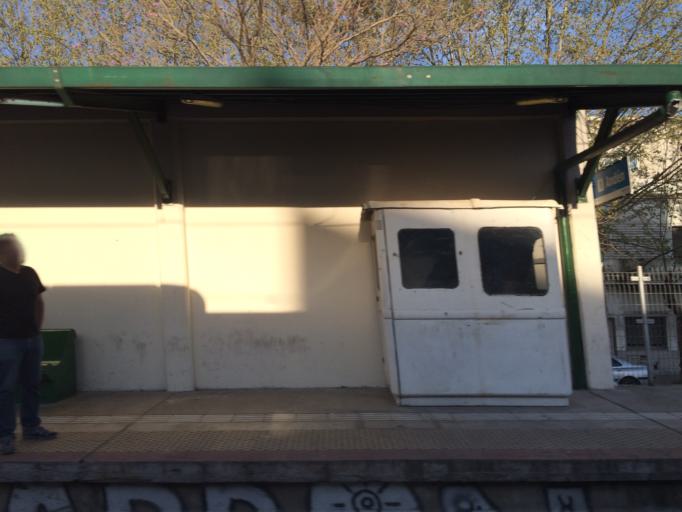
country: AR
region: Buenos Aires
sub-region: Partido de Lanus
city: Lanus
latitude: -34.7095
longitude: -58.3912
